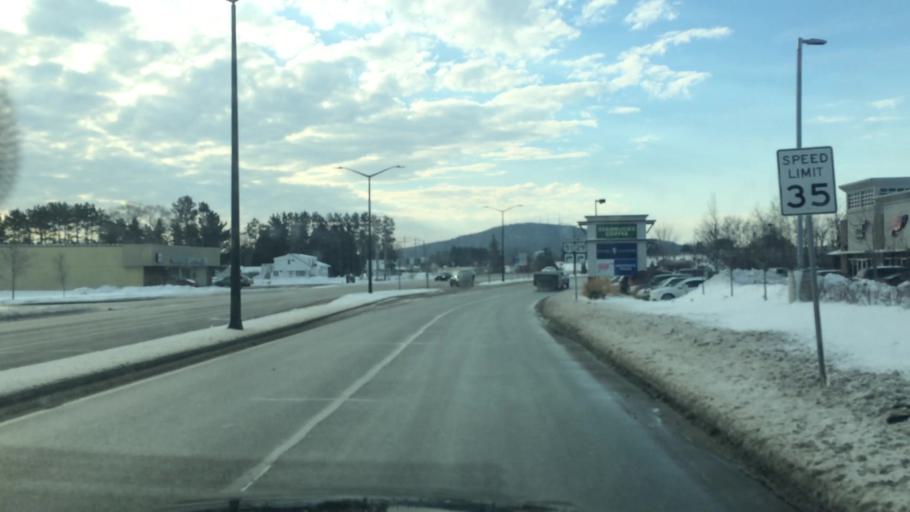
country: US
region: Wisconsin
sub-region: Marathon County
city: Rib Mountain
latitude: 44.9141
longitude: -89.6496
